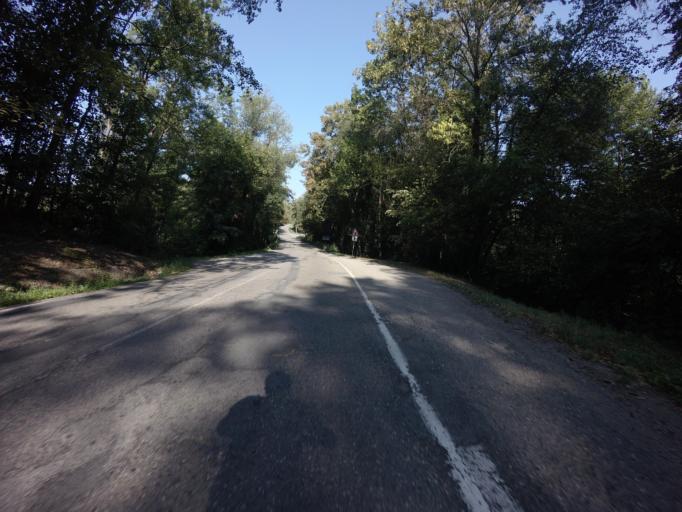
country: CZ
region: Central Bohemia
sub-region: Okres Benesov
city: Benesov
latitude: 49.7938
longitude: 14.6655
